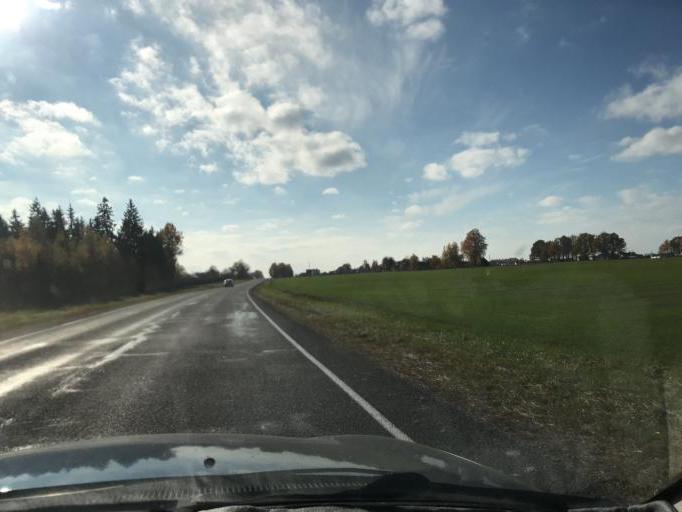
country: BY
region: Grodnenskaya
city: Voranava
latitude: 54.1729
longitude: 25.3329
